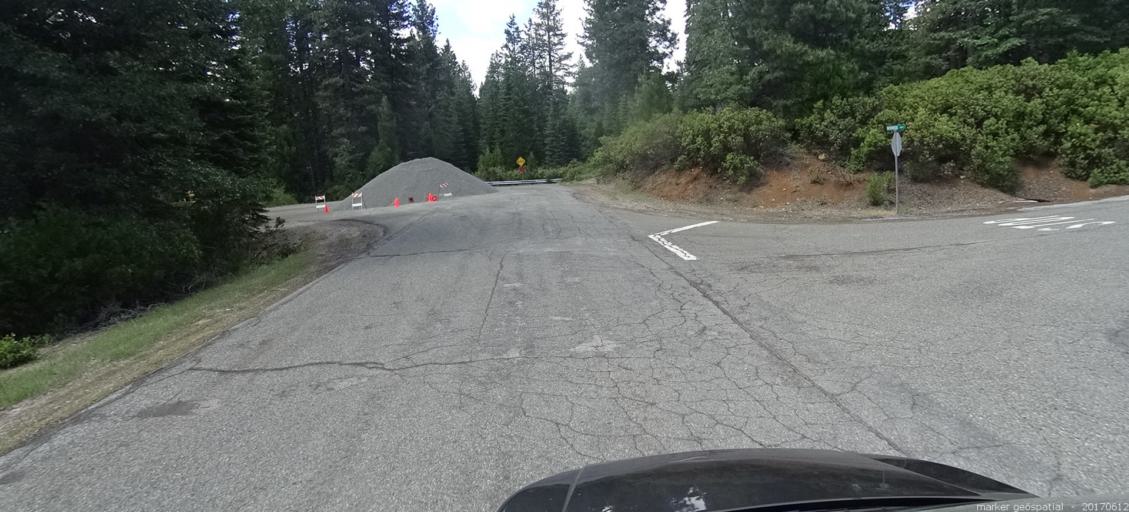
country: US
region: California
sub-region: Siskiyou County
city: Mount Shasta
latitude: 41.3191
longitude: -122.2930
